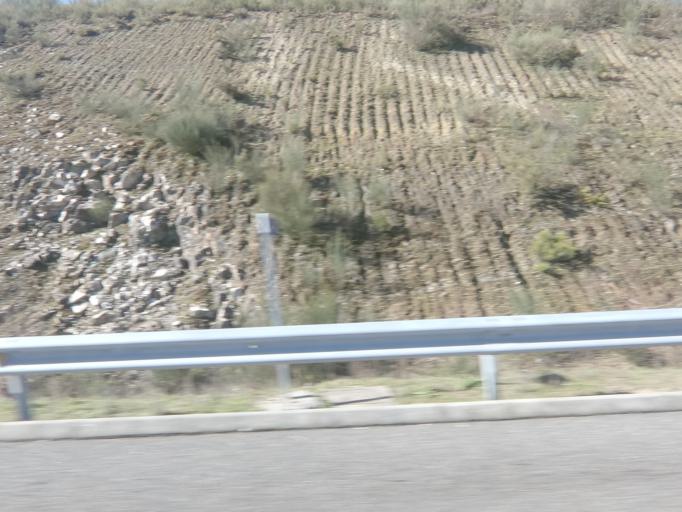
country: ES
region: Galicia
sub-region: Provincia de Pontevedra
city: Dozon
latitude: 42.5518
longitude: -8.0183
